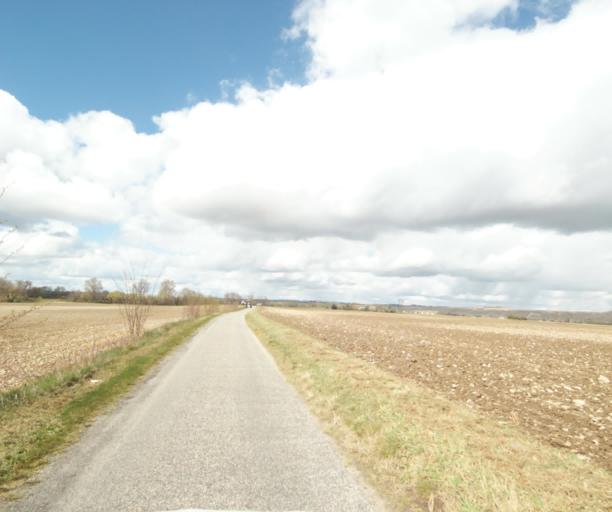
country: FR
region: Midi-Pyrenees
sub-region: Departement de l'Ariege
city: Saverdun
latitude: 43.2725
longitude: 1.5808
